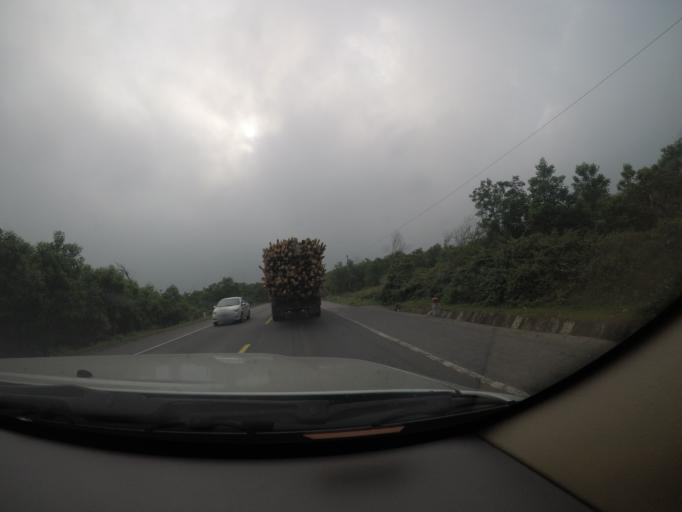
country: VN
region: Ha Tinh
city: Ky Anh
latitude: 18.0385
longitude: 106.2997
